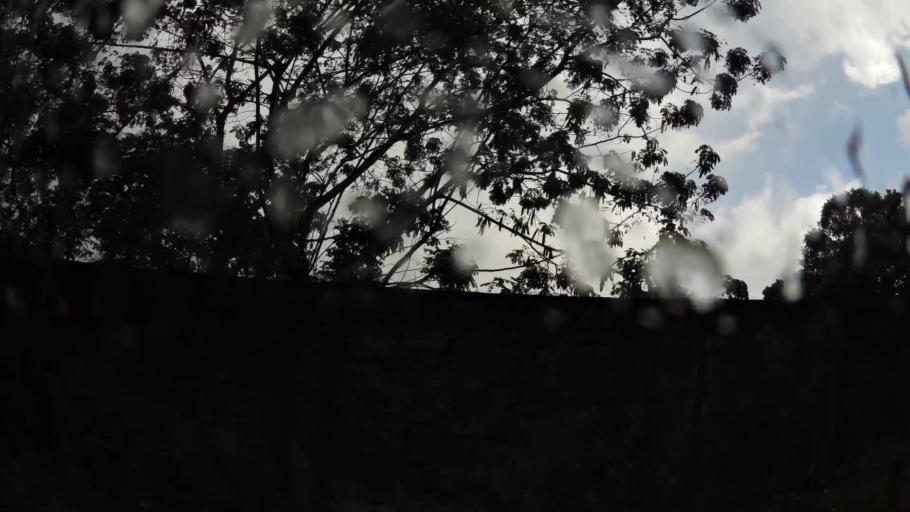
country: MQ
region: Martinique
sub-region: Martinique
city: Les Trois-Ilets
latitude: 14.5403
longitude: -61.0411
